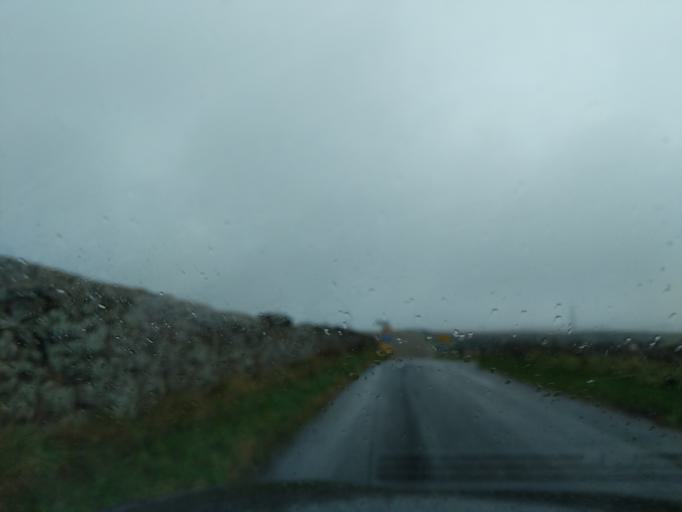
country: GB
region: Scotland
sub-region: East Lothian
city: Dunbar
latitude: 55.9567
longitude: -2.4328
